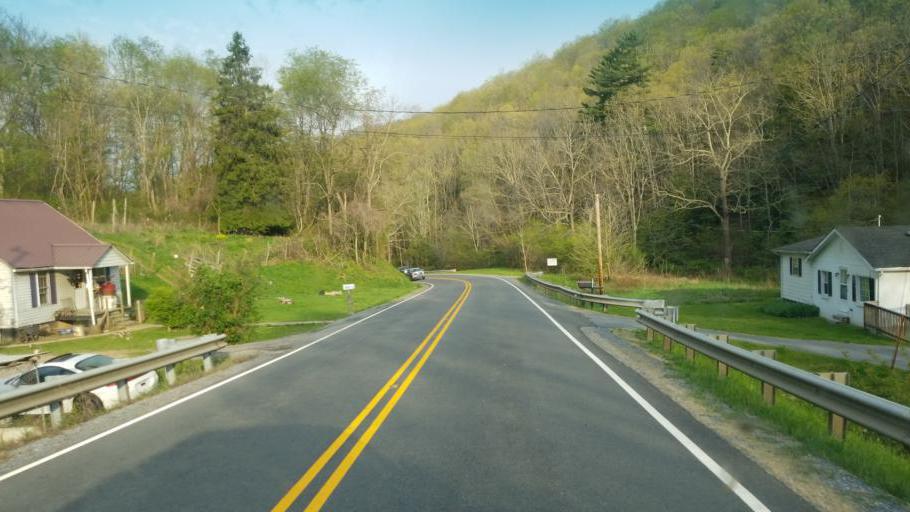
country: US
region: Virginia
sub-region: Smyth County
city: Atkins
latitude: 36.8172
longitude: -81.4488
